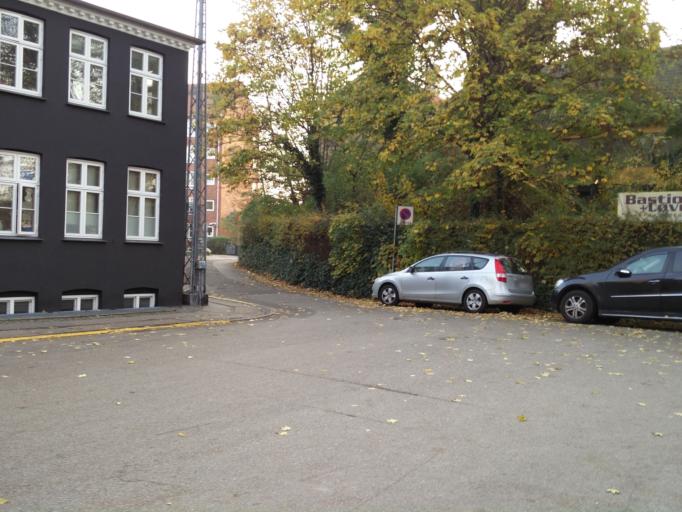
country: DK
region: Capital Region
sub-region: Kobenhavn
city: Christianshavn
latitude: 55.6717
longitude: 12.5954
